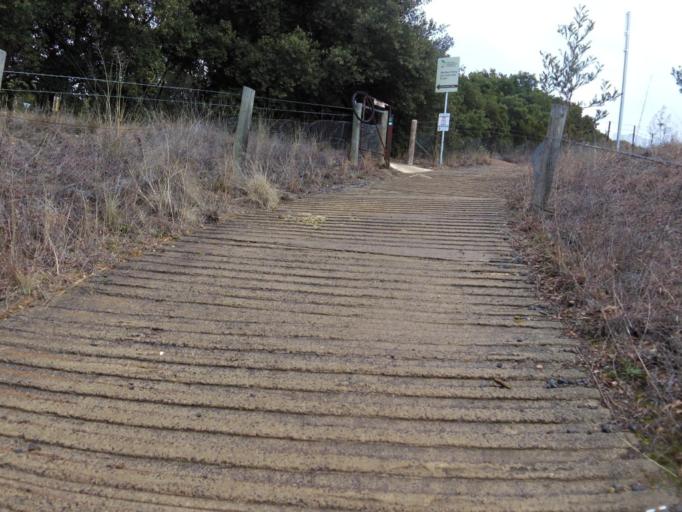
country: AU
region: Australian Capital Territory
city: Macquarie
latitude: -35.2791
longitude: 149.0810
